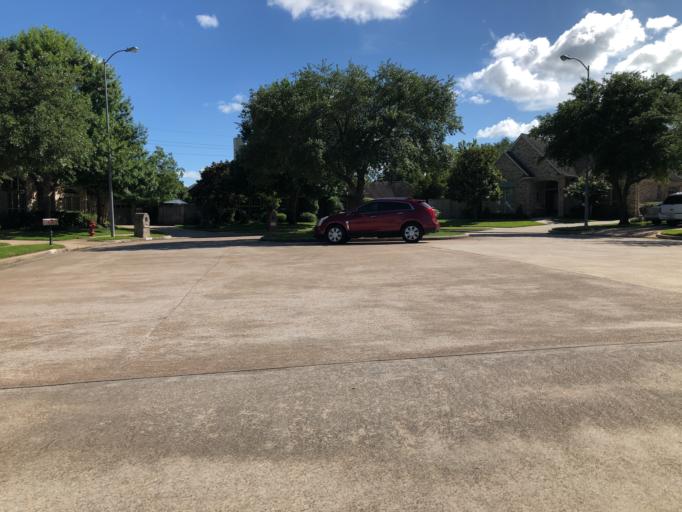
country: US
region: Texas
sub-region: Harris County
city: Katy
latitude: 29.8058
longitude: -95.8308
